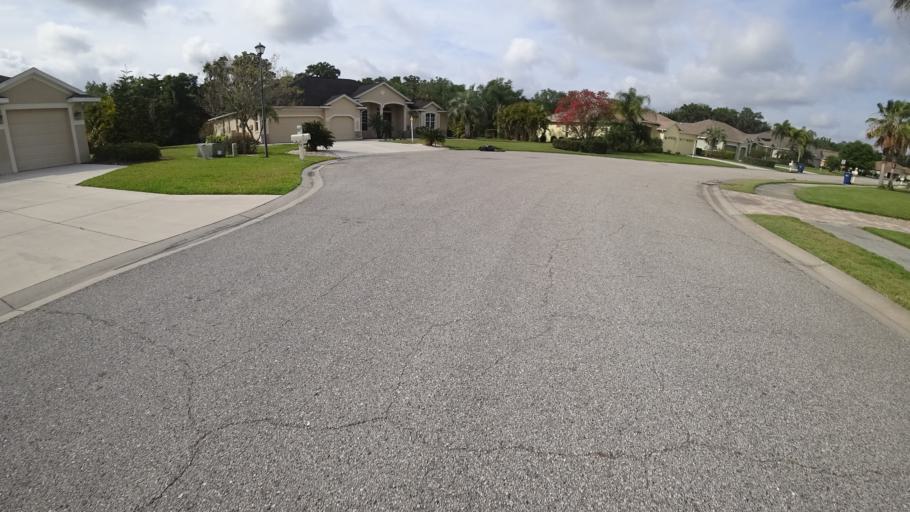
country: US
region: Florida
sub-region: Manatee County
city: Ellenton
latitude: 27.5621
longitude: -82.4677
